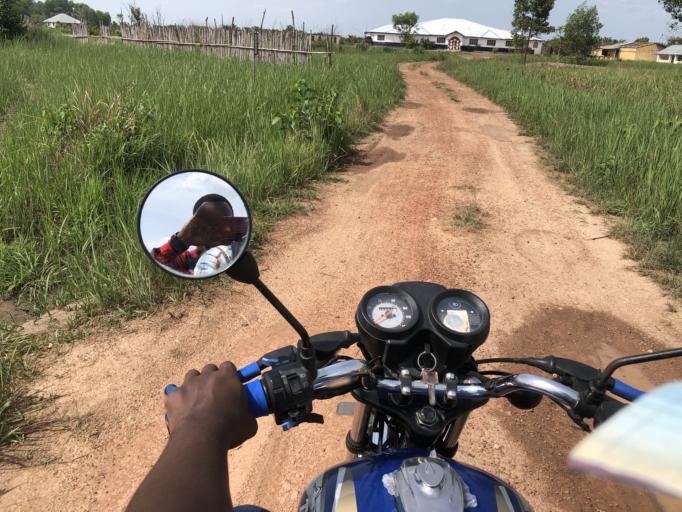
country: SL
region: Northern Province
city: Yonibana
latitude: 8.4711
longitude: -12.2336
